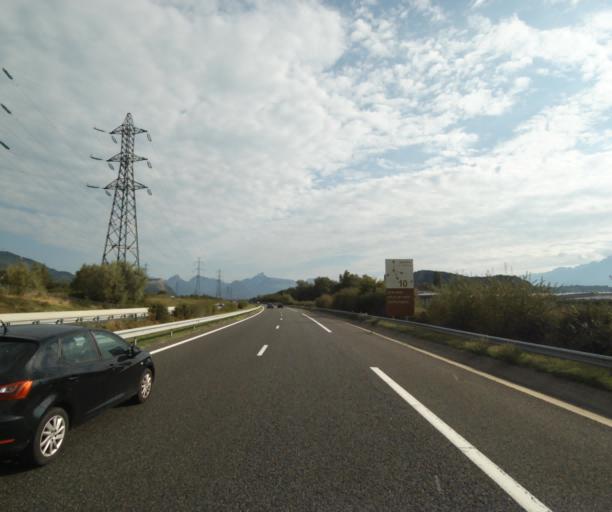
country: FR
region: Rhone-Alpes
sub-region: Departement de l'Isere
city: Allieres-et-Risset
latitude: 45.0991
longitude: 5.6743
